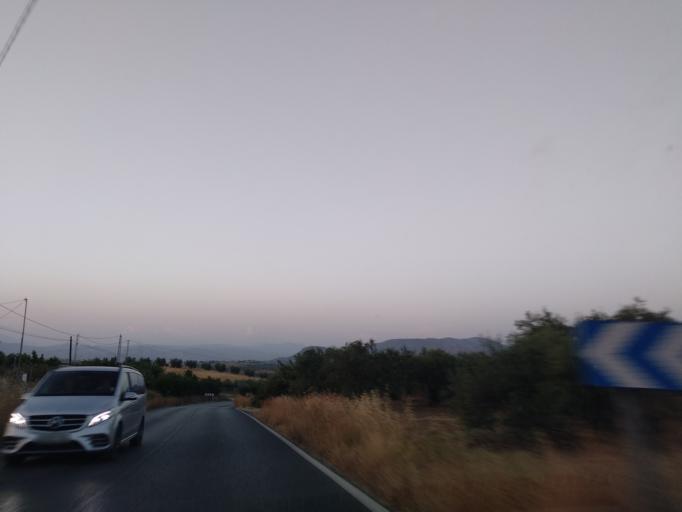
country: ES
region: Andalusia
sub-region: Provincia de Malaga
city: Alhaurin el Grande
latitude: 36.6613
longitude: -4.6719
